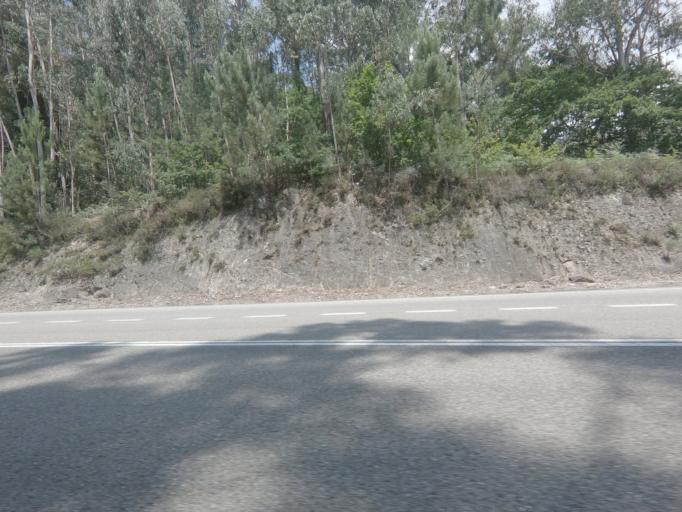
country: ES
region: Galicia
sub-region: Provincia de Pontevedra
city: Tomino
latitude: 42.0462
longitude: -8.7281
